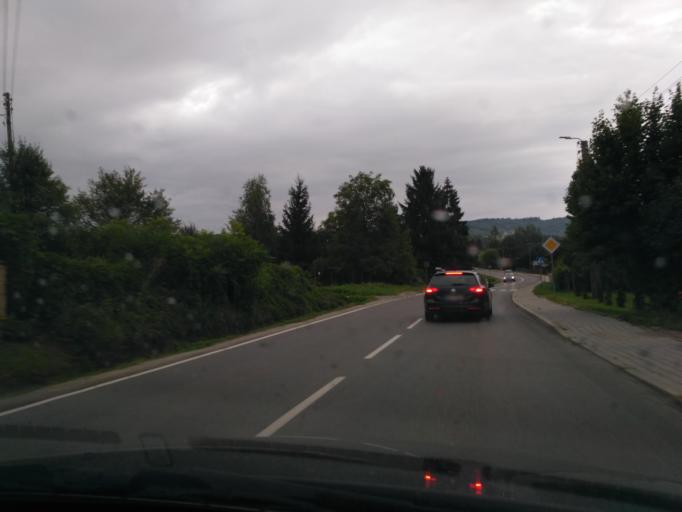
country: PL
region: Subcarpathian Voivodeship
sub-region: Powiat krosnienski
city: Korczyna
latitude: 49.7178
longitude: 21.8108
